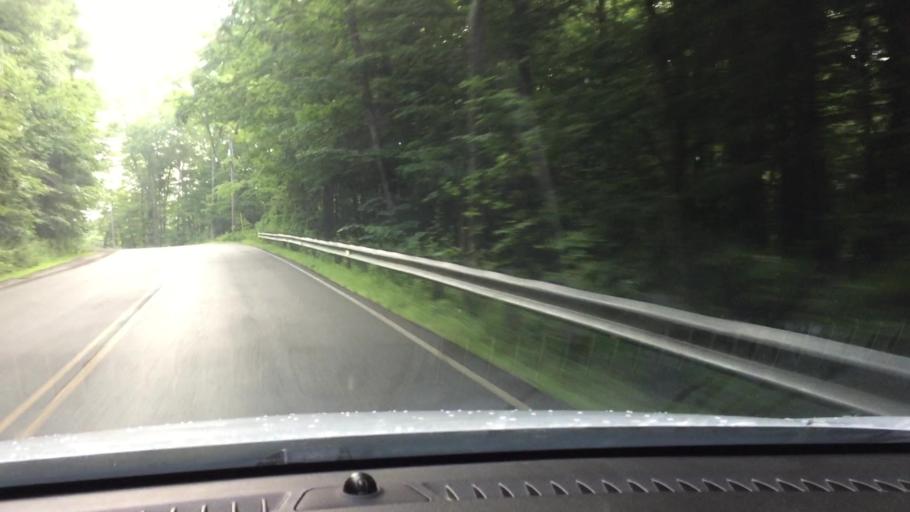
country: US
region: Massachusetts
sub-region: Hampshire County
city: Westhampton
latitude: 42.2594
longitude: -72.9084
